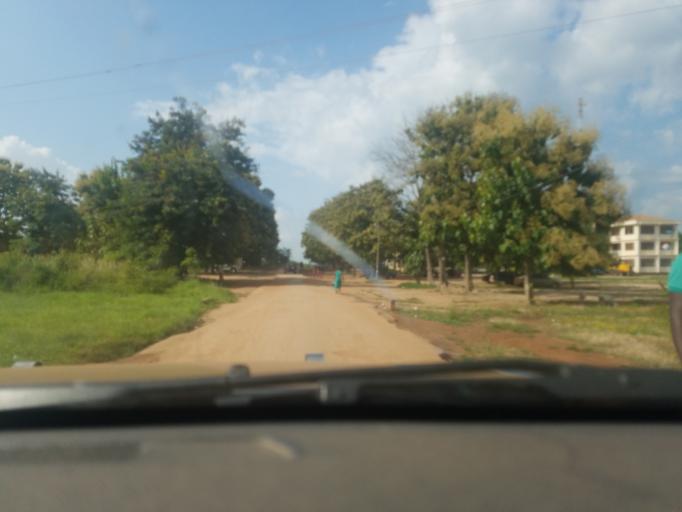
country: GH
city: Duayaw Nkwanta
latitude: 6.9788
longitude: -2.3831
